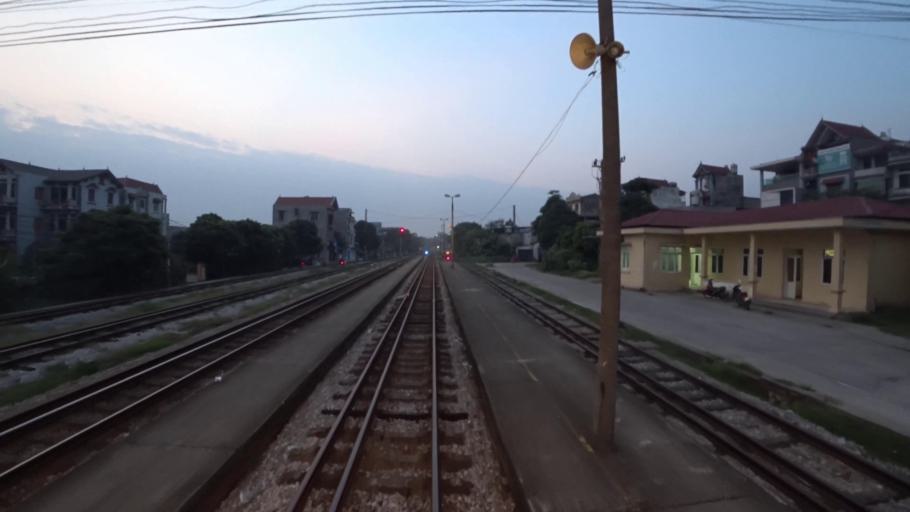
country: VN
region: Ha Noi
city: Soc Son
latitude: 21.2414
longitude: 105.8614
